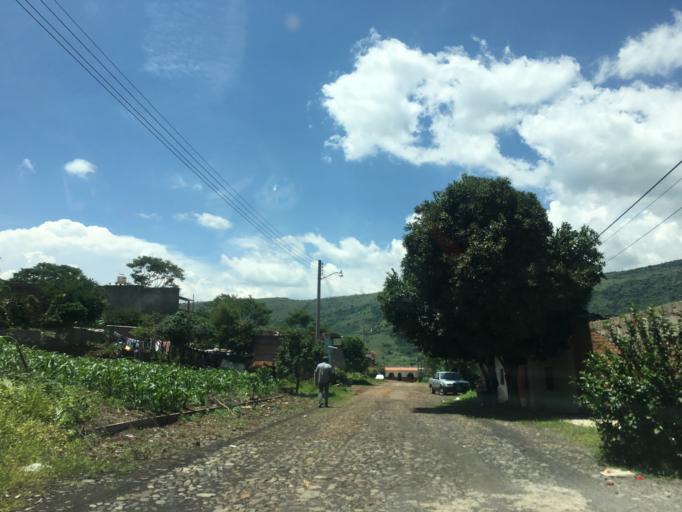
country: MX
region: Nayarit
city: Ixtlan del Rio
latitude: 21.0374
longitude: -104.3512
